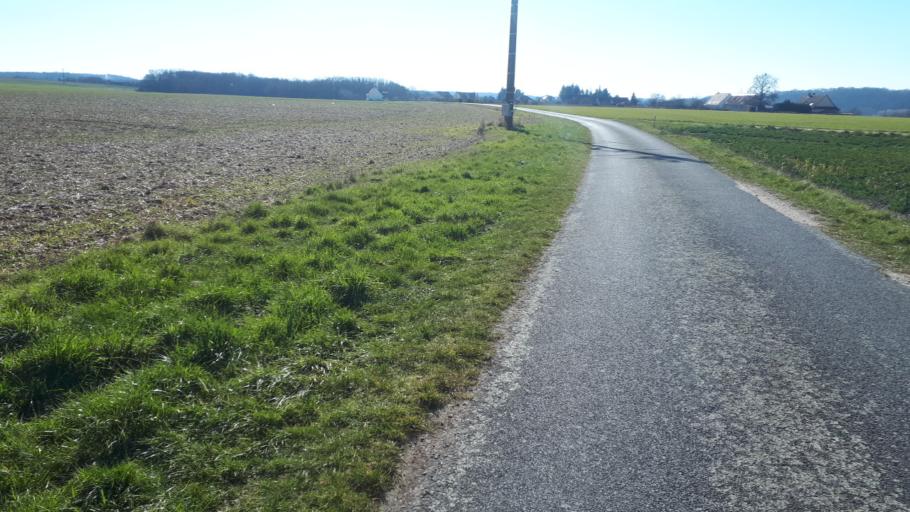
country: FR
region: Centre
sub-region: Departement du Loir-et-Cher
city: Villiers-sur-Loir
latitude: 47.7945
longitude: 0.9715
